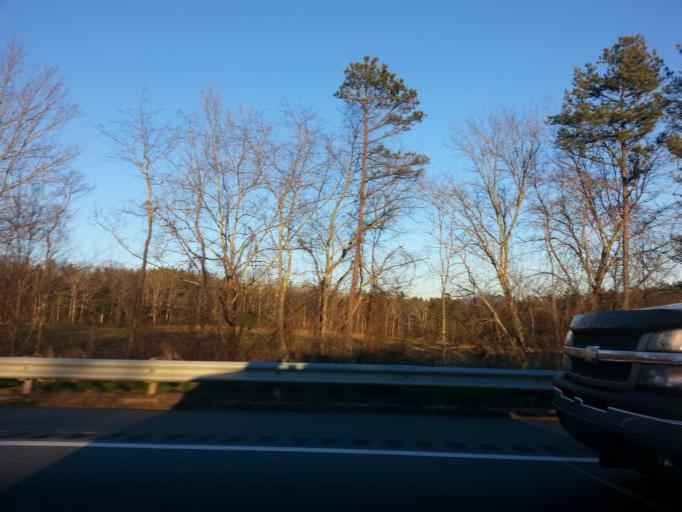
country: US
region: North Carolina
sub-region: Buncombe County
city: Bent Creek
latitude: 35.5298
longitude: -82.5999
